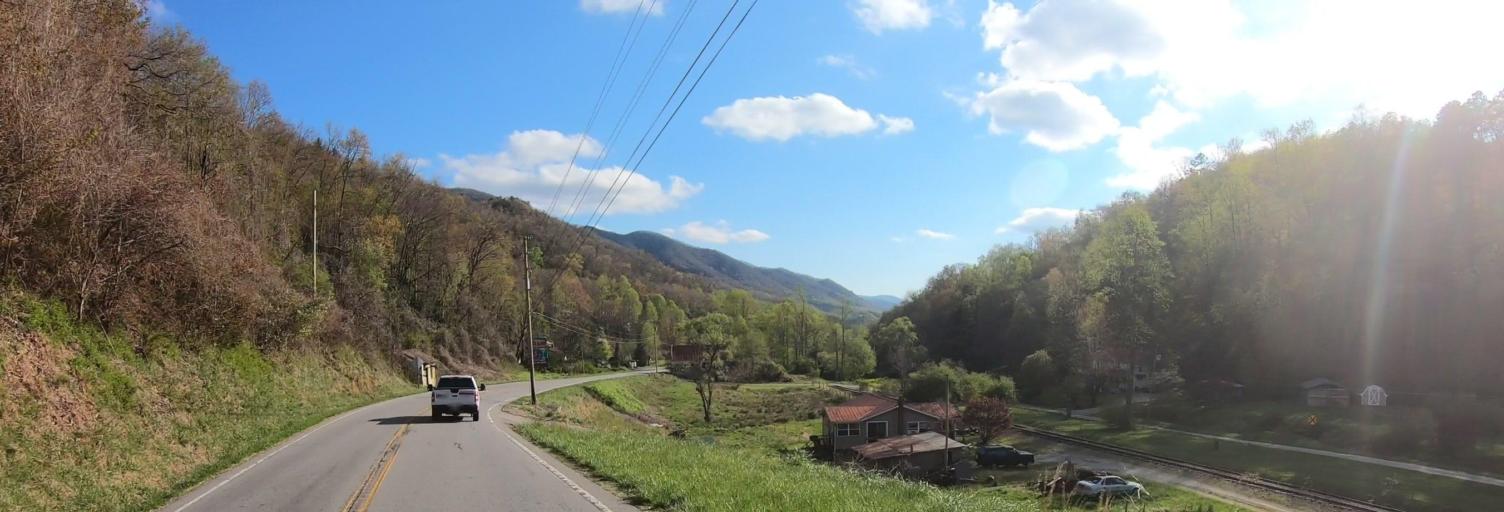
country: US
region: North Carolina
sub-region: Cherokee County
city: Andrews
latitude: 35.2467
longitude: -83.7034
